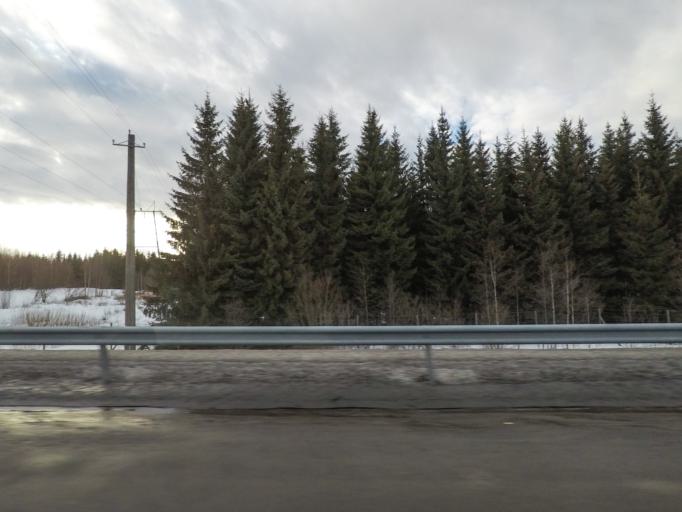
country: FI
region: Paijanne Tavastia
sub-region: Lahti
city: Heinola
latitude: 61.1252
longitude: 25.9369
